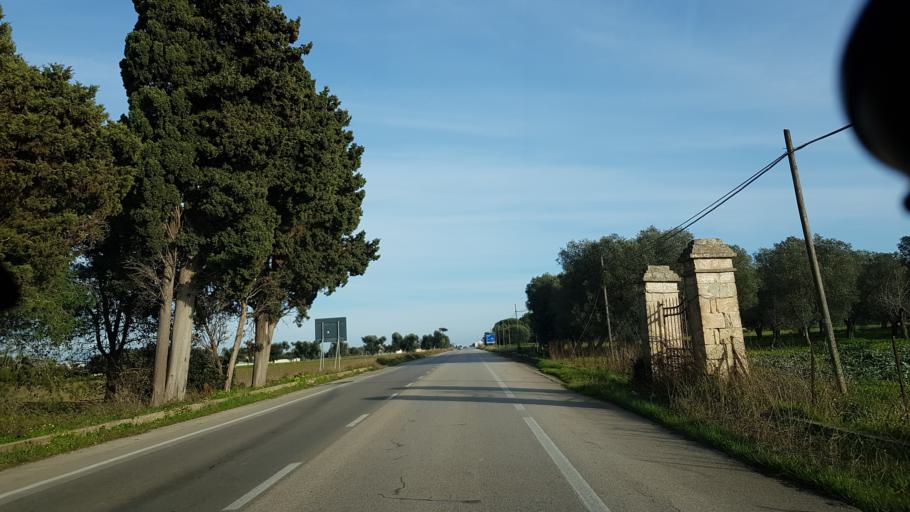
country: IT
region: Apulia
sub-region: Provincia di Brindisi
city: Brindisi
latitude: 40.6458
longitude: 17.9018
